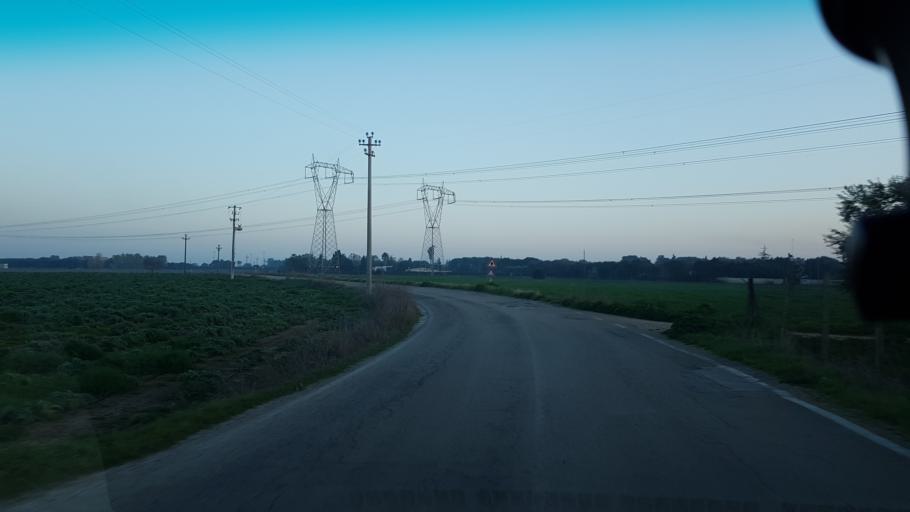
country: IT
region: Apulia
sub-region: Provincia di Brindisi
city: Mesagne
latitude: 40.5854
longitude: 17.7987
